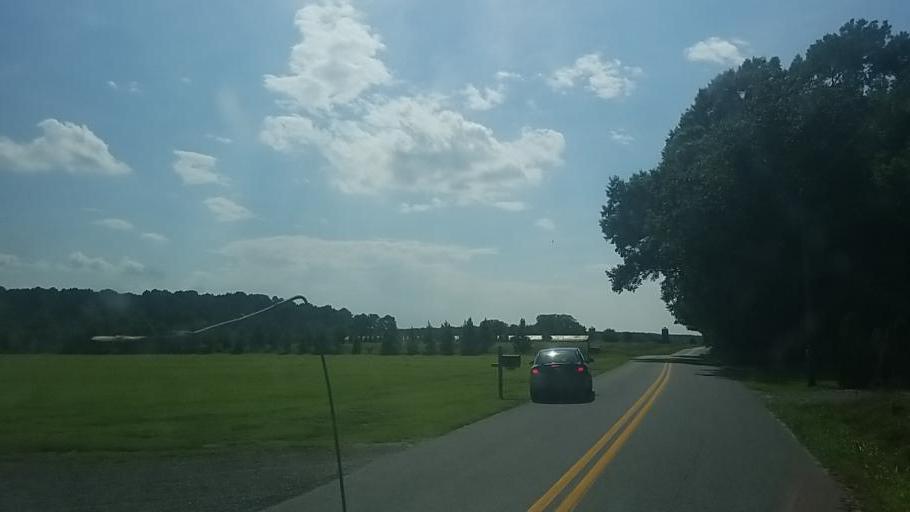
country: US
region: Maryland
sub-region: Somerset County
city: Princess Anne
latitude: 38.2615
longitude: -75.6766
